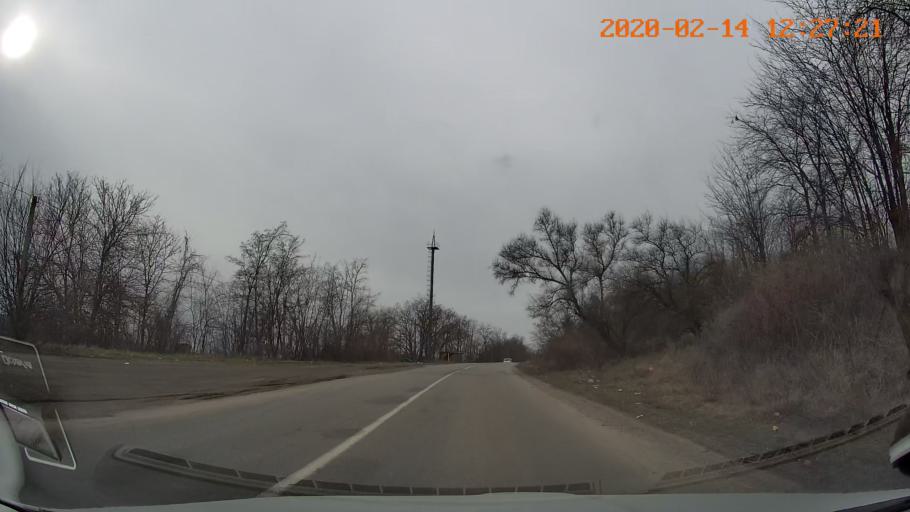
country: RO
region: Botosani
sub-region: Comuna Paltinis
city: Paltinis
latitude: 48.2608
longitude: 26.6098
